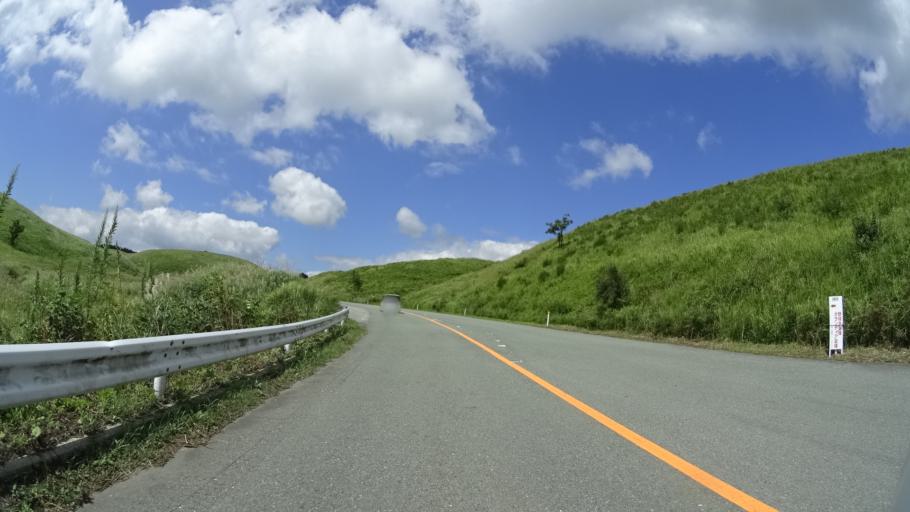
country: JP
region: Kumamoto
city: Aso
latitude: 33.0040
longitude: 131.1295
